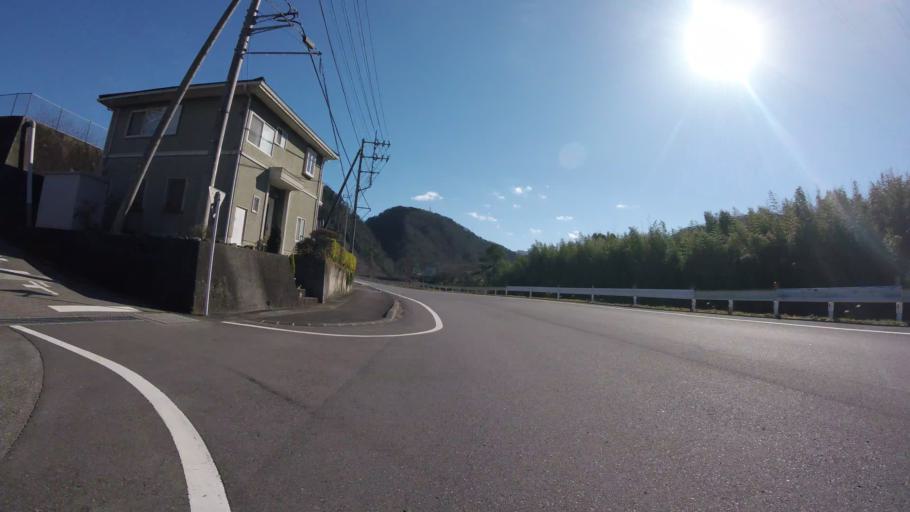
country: JP
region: Shizuoka
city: Heda
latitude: 34.9399
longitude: 138.9320
